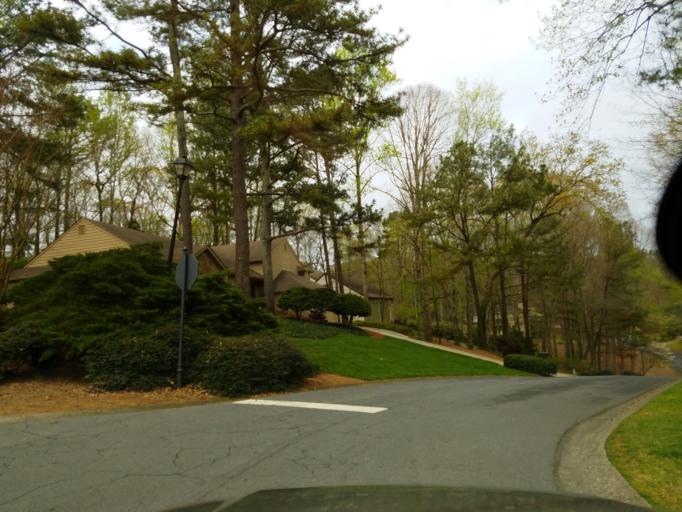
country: US
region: Georgia
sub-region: Fulton County
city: Roswell
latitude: 34.0314
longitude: -84.4244
